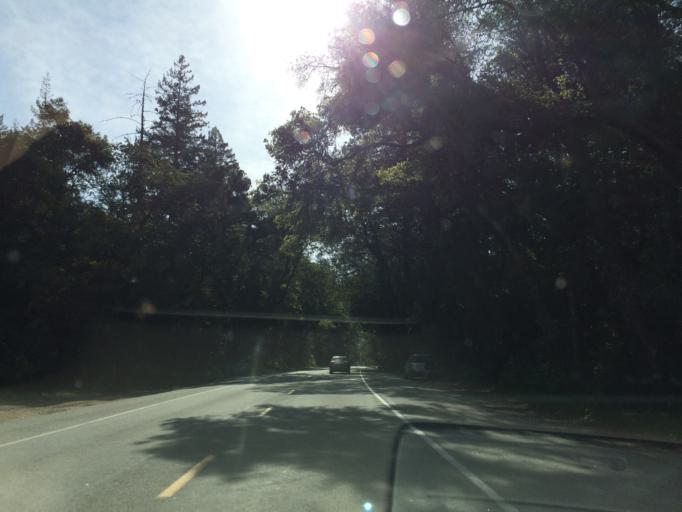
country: US
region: California
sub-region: Santa Cruz County
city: Felton
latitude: 37.0213
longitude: -122.0845
